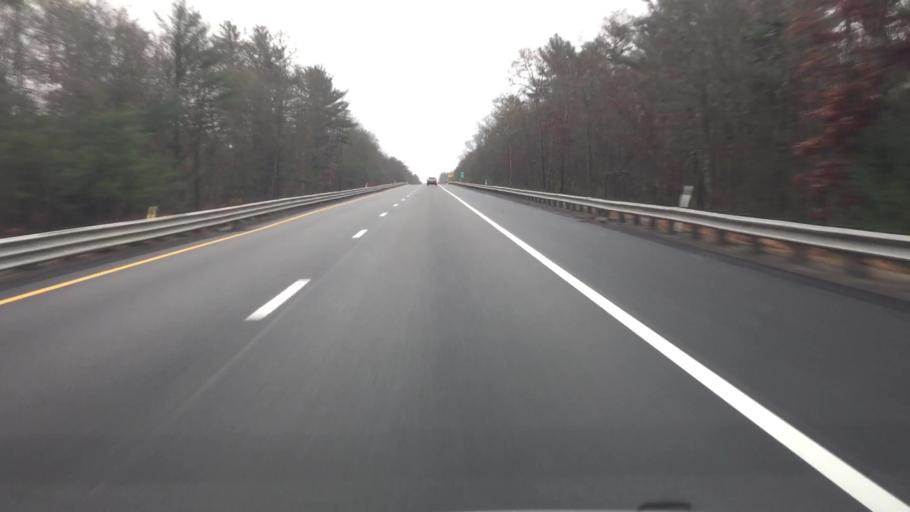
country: US
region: Massachusetts
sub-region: Plymouth County
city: West Wareham
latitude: 41.8265
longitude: -70.8112
